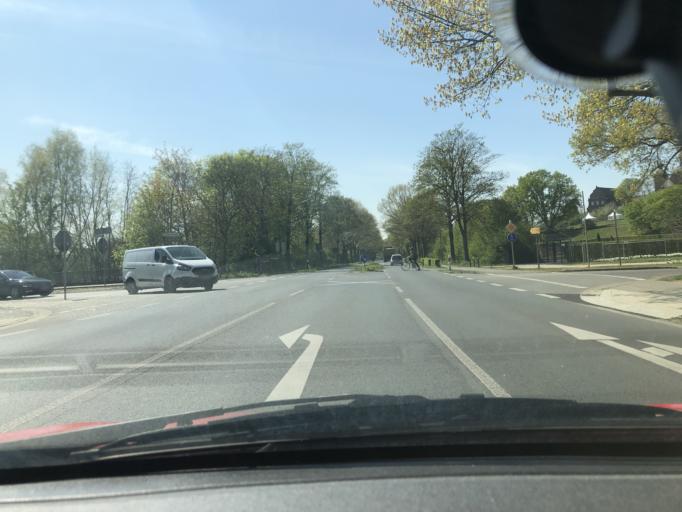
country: DE
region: North Rhine-Westphalia
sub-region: Regierungsbezirk Dusseldorf
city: Kamp-Lintfort
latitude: 51.5037
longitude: 6.5216
